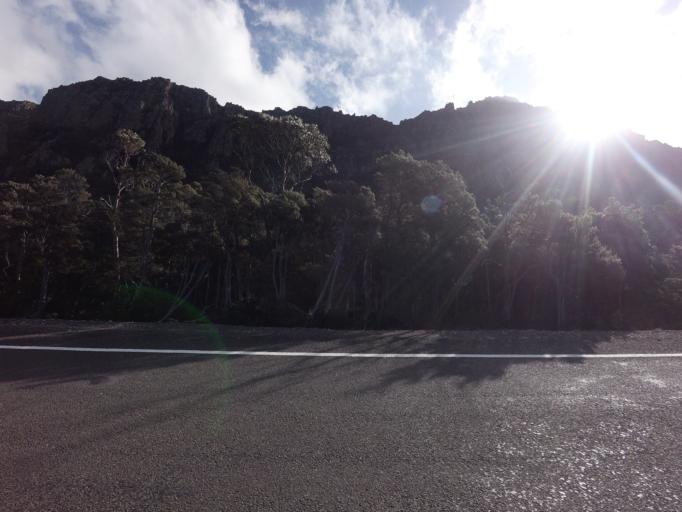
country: AU
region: Tasmania
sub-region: Meander Valley
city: Deloraine
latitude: -41.7210
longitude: 146.7247
